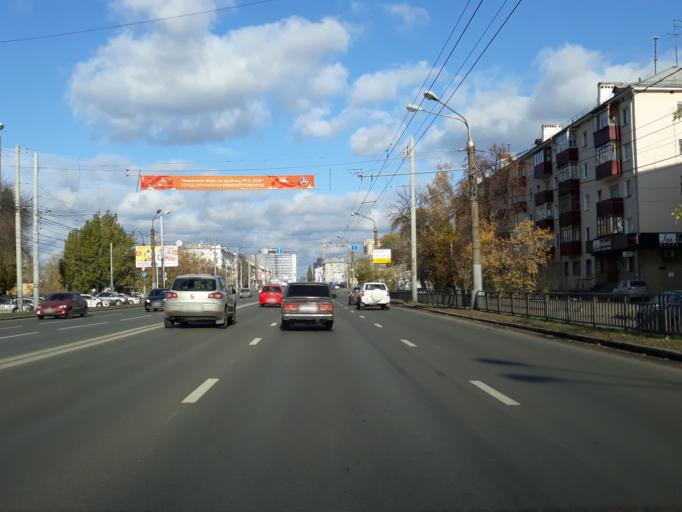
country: RU
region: Nizjnij Novgorod
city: Nizhniy Novgorod
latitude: 56.2943
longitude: 43.9348
